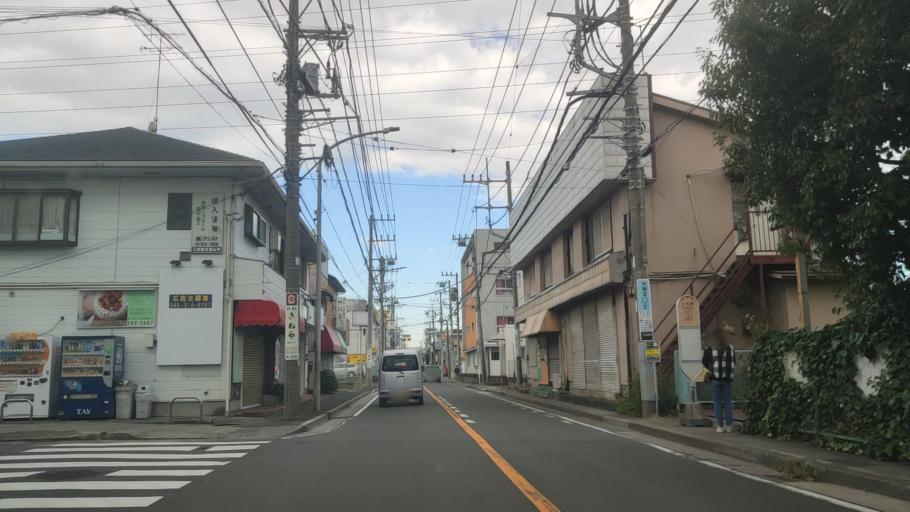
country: JP
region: Kanagawa
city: Fujisawa
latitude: 35.4217
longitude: 139.5339
